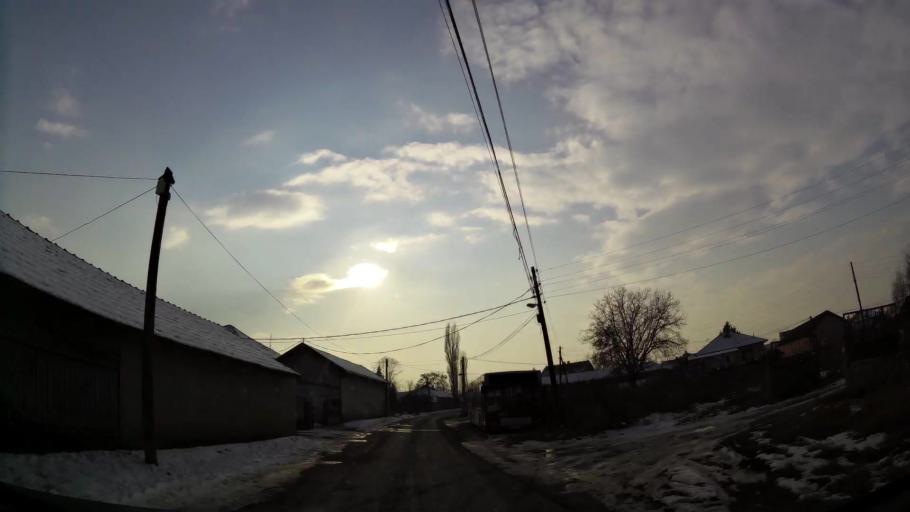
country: MK
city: Creshevo
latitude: 42.0272
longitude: 21.5112
